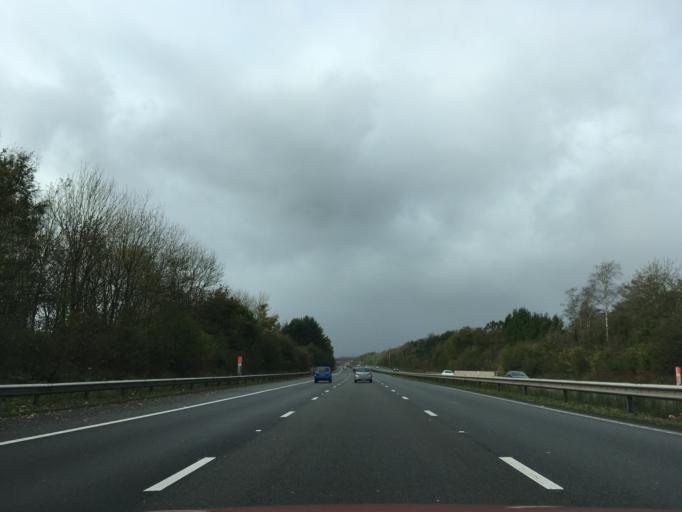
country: GB
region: Wales
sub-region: Caerphilly County Borough
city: Machen
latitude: 51.5464
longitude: -3.1631
